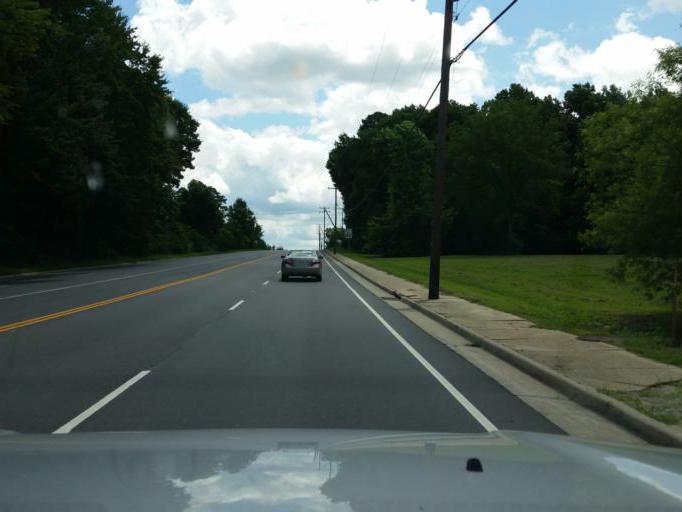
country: US
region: Virginia
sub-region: City of Williamsburg
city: Williamsburg
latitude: 37.2594
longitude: -76.6726
